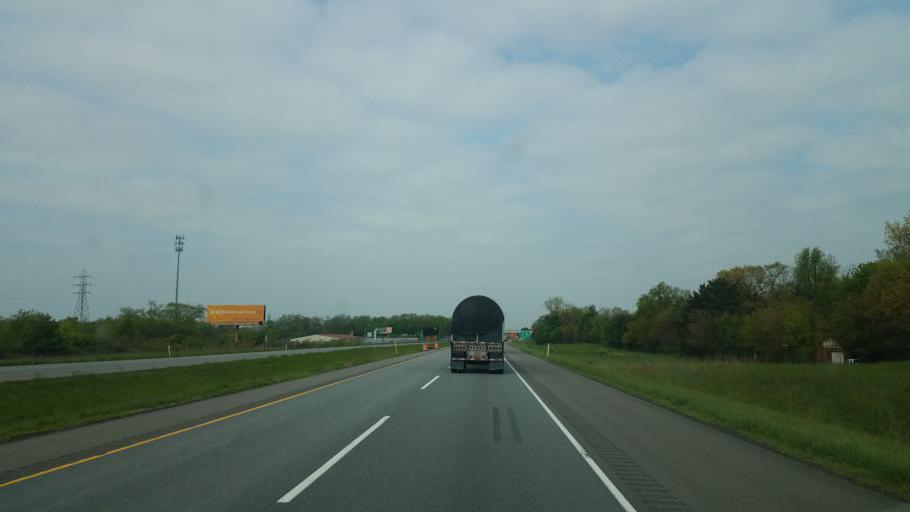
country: US
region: Indiana
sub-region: Saint Joseph County
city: Georgetown
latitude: 41.7160
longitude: -86.2096
